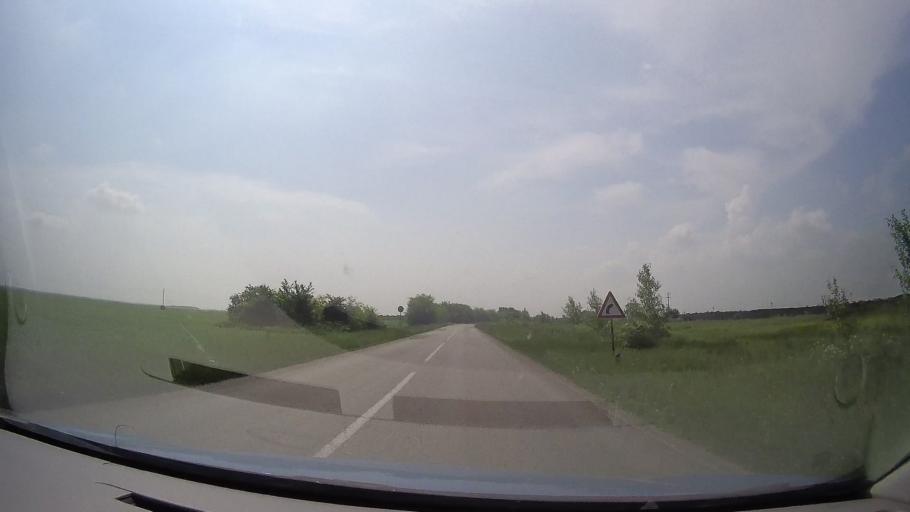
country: RS
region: Autonomna Pokrajina Vojvodina
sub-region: Juznobanatski Okrug
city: Kovacica
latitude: 45.0839
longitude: 20.6394
